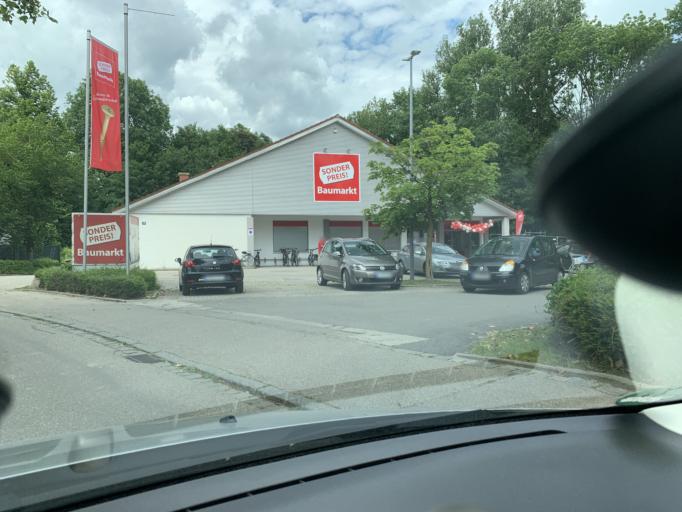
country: DE
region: Bavaria
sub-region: Upper Bavaria
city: Moosburg
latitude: 48.4760
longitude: 11.9474
